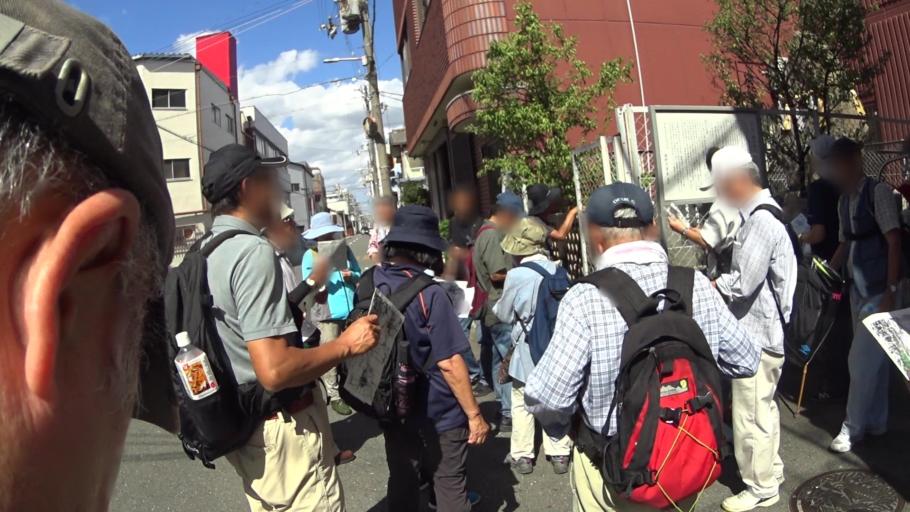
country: JP
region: Osaka
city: Yao
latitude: 34.6455
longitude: 135.5457
